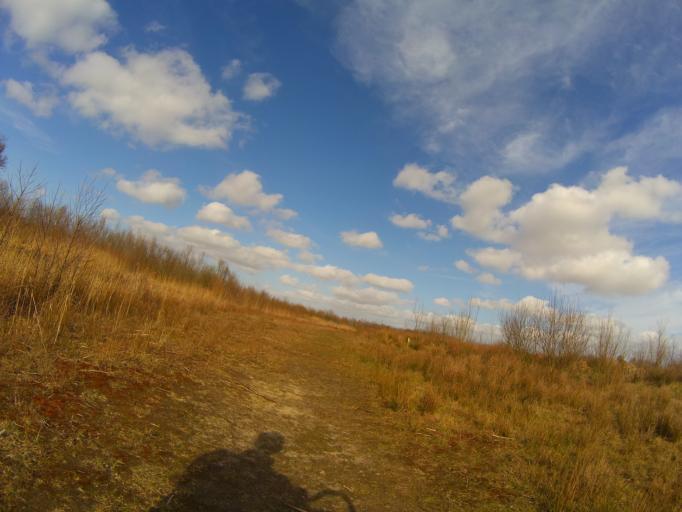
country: NL
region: Utrecht
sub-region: Gemeente Amersfoort
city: Randenbroek
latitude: 52.1560
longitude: 5.4220
